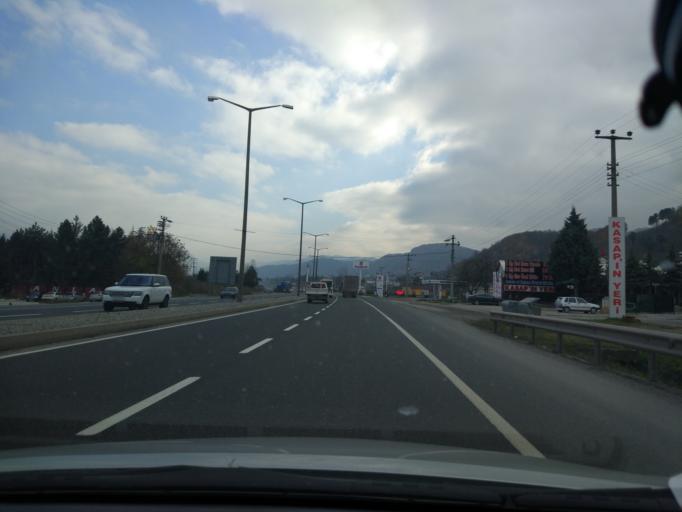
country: TR
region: Duzce
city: Kaynasli
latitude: 40.7799
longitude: 31.2829
